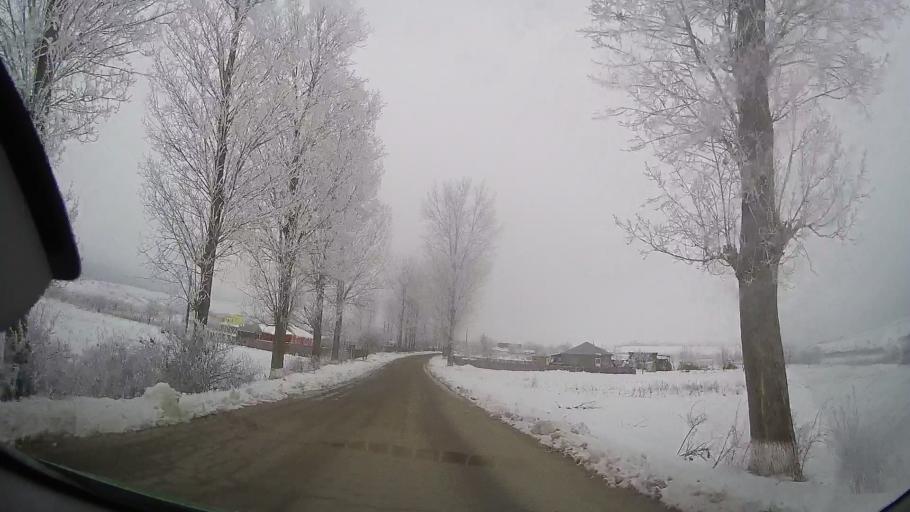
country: RO
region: Iasi
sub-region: Comuna Tansa
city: Tansa
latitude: 46.9134
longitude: 27.2108
